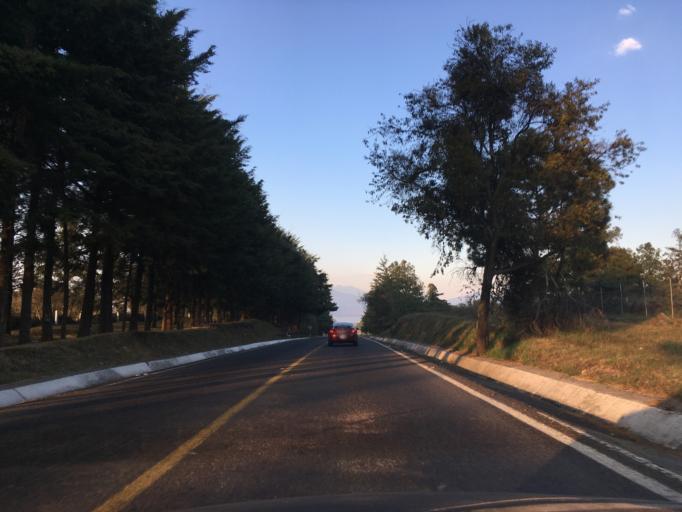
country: MX
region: Michoacan
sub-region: Patzcuaro
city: Santa Ana Chapitiro
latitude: 19.5144
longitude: -101.6677
